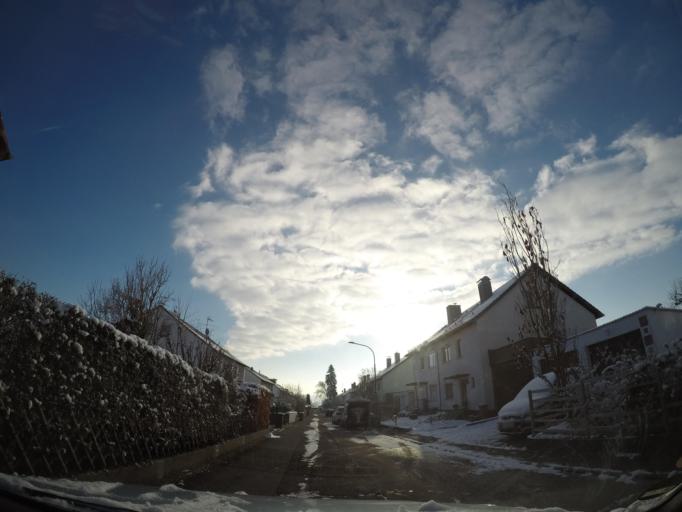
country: DE
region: Bavaria
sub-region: Swabia
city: Senden
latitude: 48.3165
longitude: 10.0621
